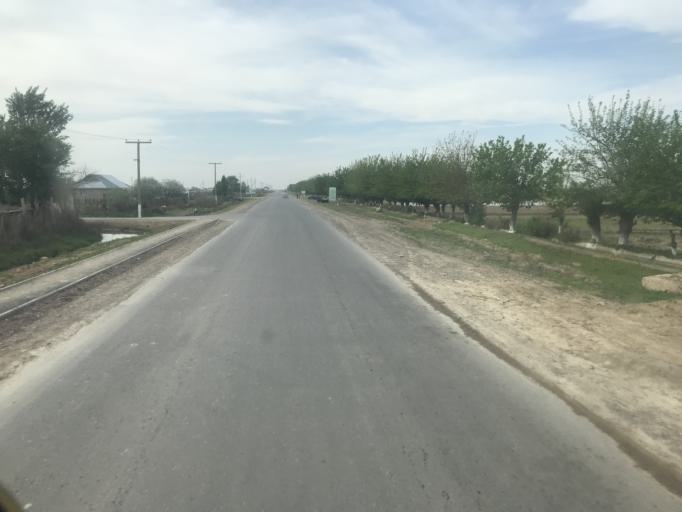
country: KZ
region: Ongtustik Qazaqstan
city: Asykata
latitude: 40.9910
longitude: 68.2099
